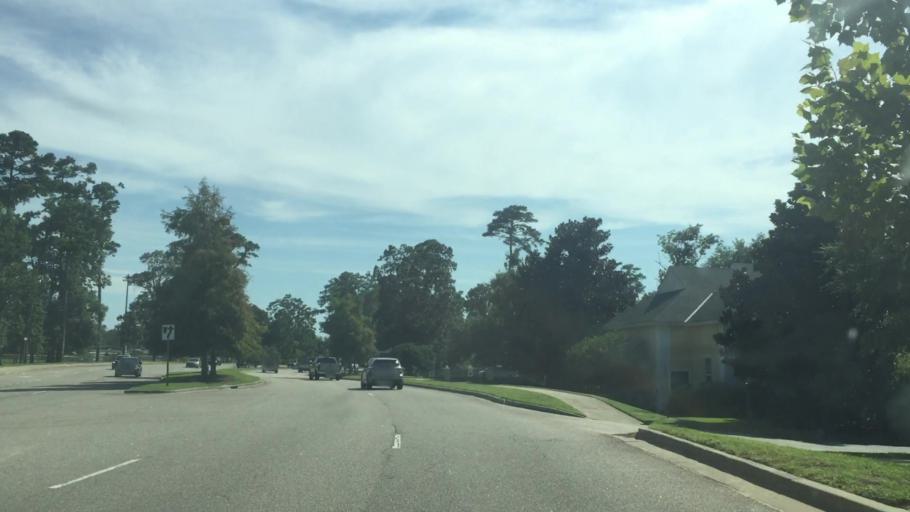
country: US
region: South Carolina
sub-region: Horry County
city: Myrtle Beach
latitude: 33.7195
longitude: -78.8696
